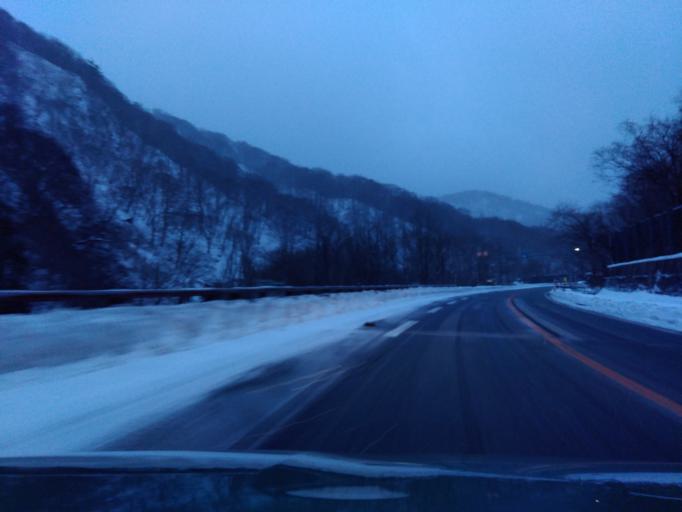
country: JP
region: Iwate
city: Shizukuishi
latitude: 39.7208
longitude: 140.8344
